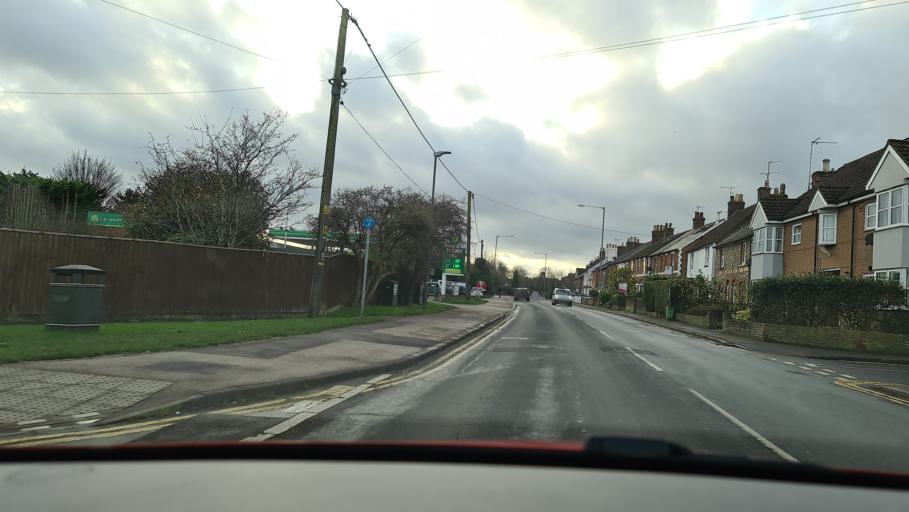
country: GB
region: England
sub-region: Buckinghamshire
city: Wendover
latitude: 51.7681
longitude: -0.7452
